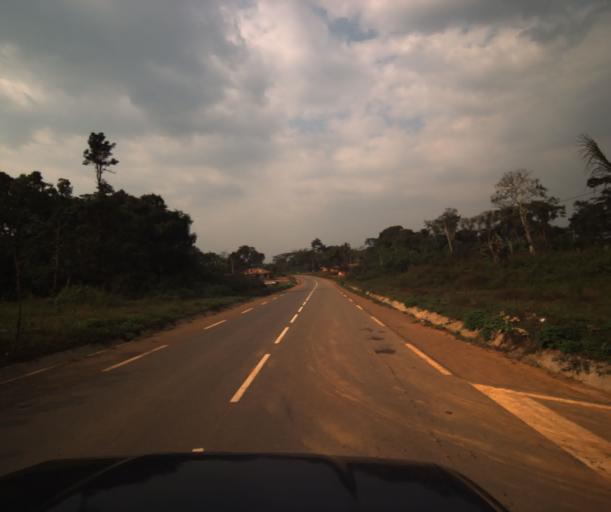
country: CM
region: Centre
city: Mbankomo
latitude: 3.7566
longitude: 11.4055
